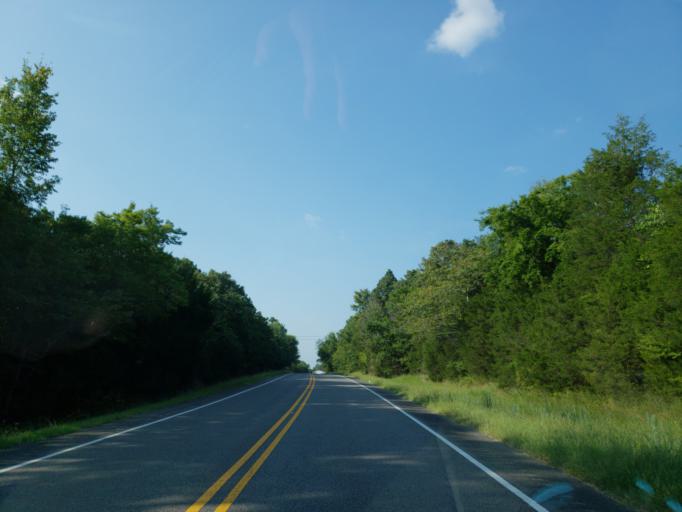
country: US
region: Alabama
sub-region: Sumter County
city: Livingston
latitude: 32.6422
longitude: -88.1716
